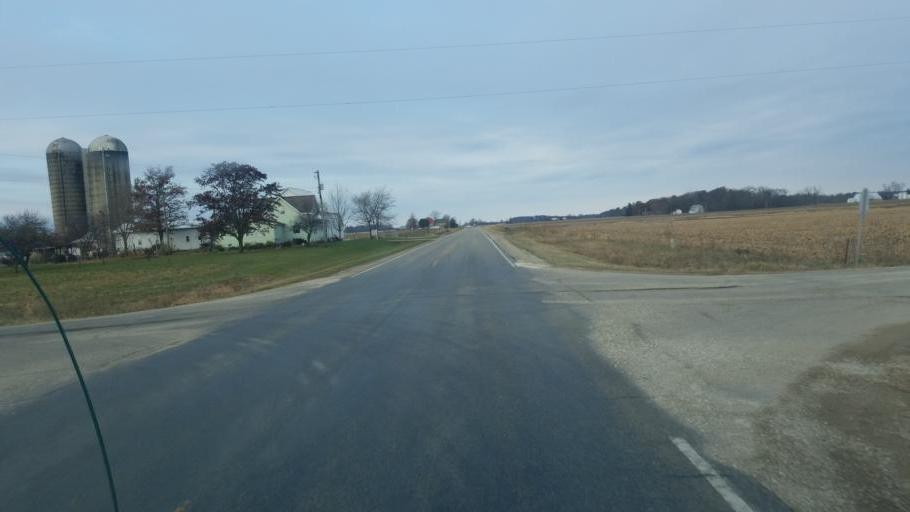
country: US
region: Indiana
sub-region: Adams County
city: Geneva
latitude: 40.5425
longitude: -84.8481
